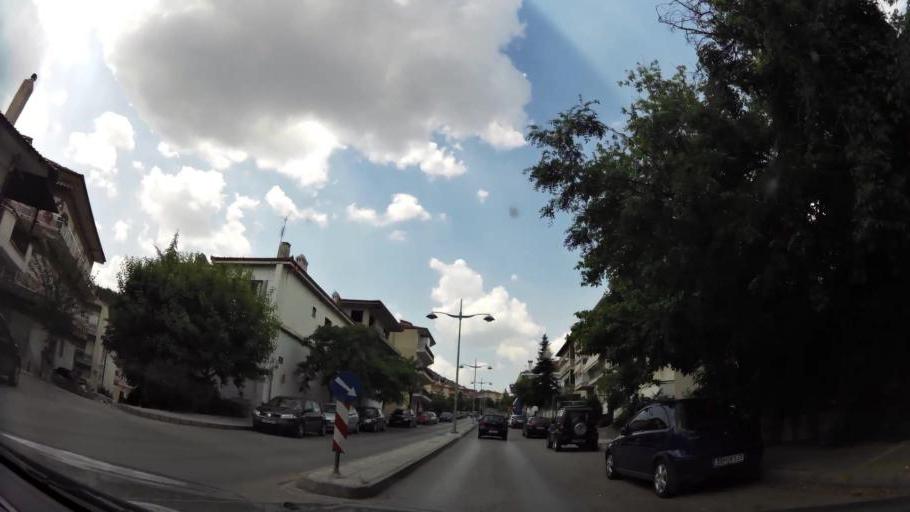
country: GR
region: West Macedonia
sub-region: Nomos Kozanis
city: Kozani
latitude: 40.3083
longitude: 21.7862
